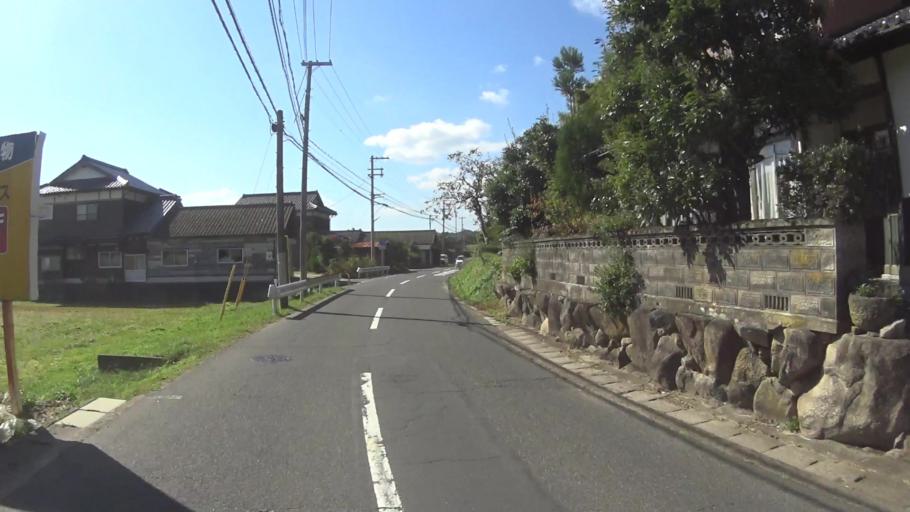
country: JP
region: Kyoto
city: Miyazu
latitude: 35.6742
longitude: 135.0815
